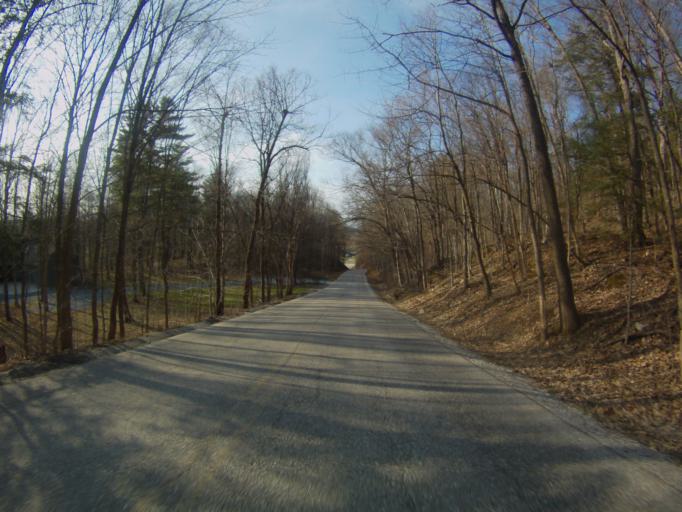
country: US
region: Vermont
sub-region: Addison County
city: Middlebury (village)
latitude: 44.0192
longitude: -73.2228
